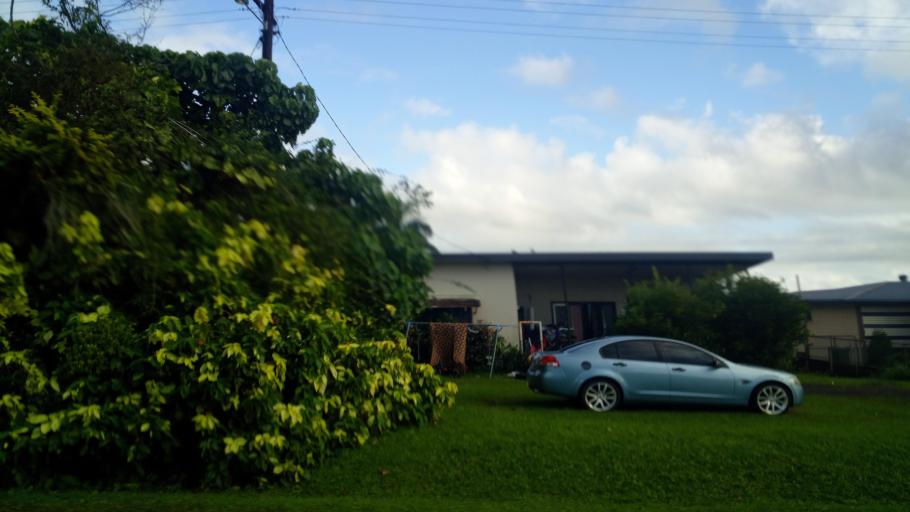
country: AU
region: Queensland
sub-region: Cassowary Coast
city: Innisfail
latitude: -17.5173
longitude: 145.9887
